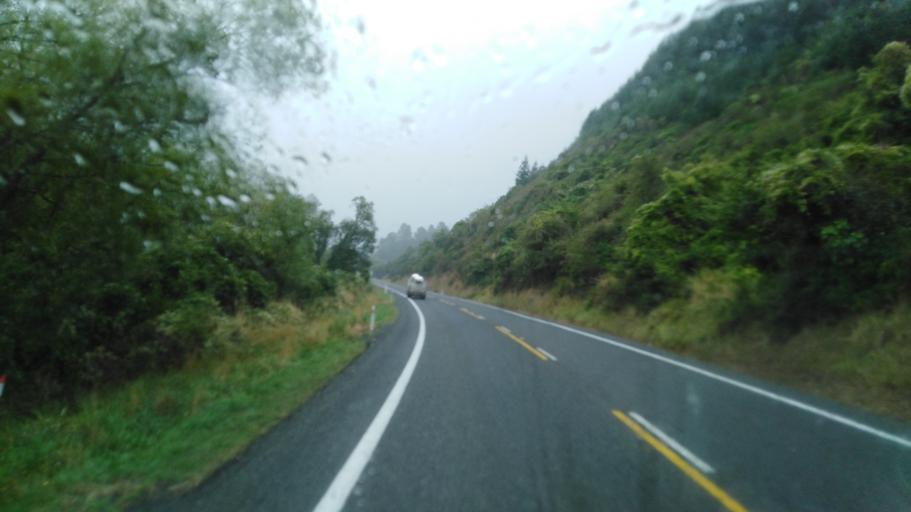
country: NZ
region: Marlborough
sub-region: Marlborough District
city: Picton
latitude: -41.3856
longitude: 173.9519
